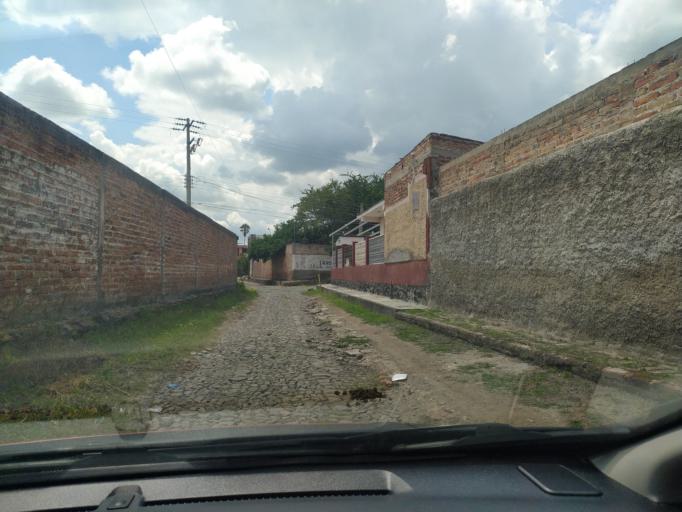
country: MX
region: Jalisco
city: Villa Corona
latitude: 20.3510
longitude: -103.6708
